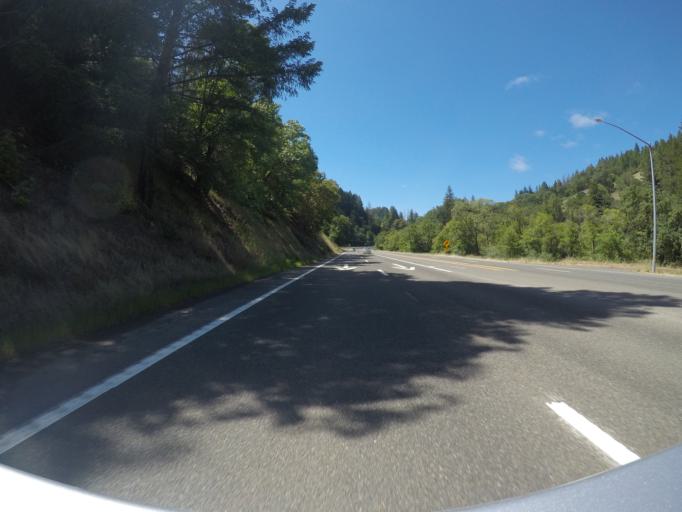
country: US
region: California
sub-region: Mendocino County
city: Brooktrails
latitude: 39.5552
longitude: -123.4303
